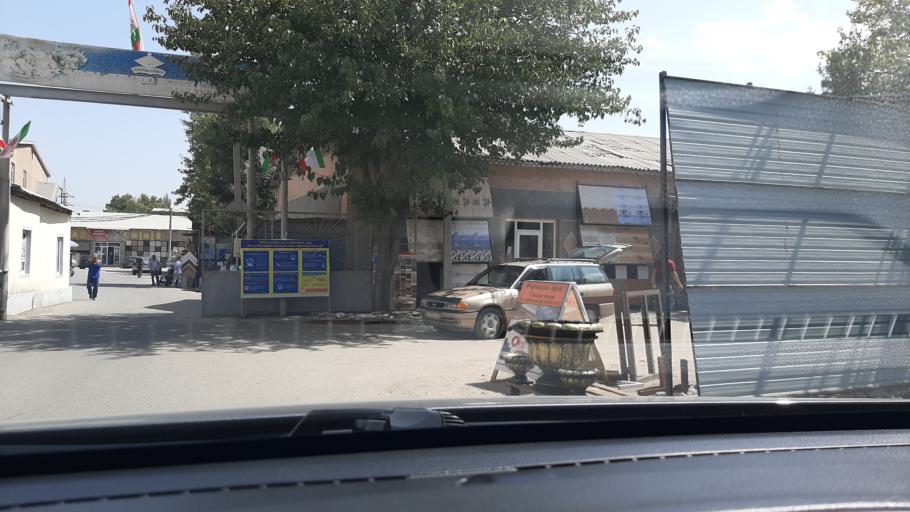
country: TJ
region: Dushanbe
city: Dushanbe
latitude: 38.5499
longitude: 68.7750
